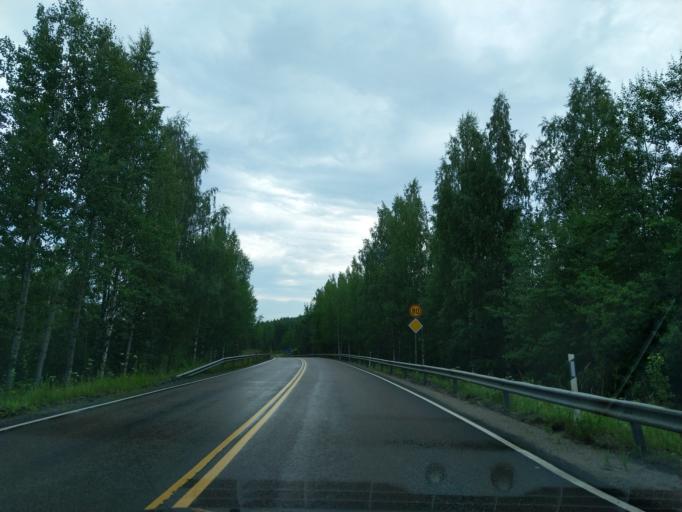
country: FI
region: Southern Savonia
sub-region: Savonlinna
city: Punkaharju
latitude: 61.6793
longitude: 29.4134
